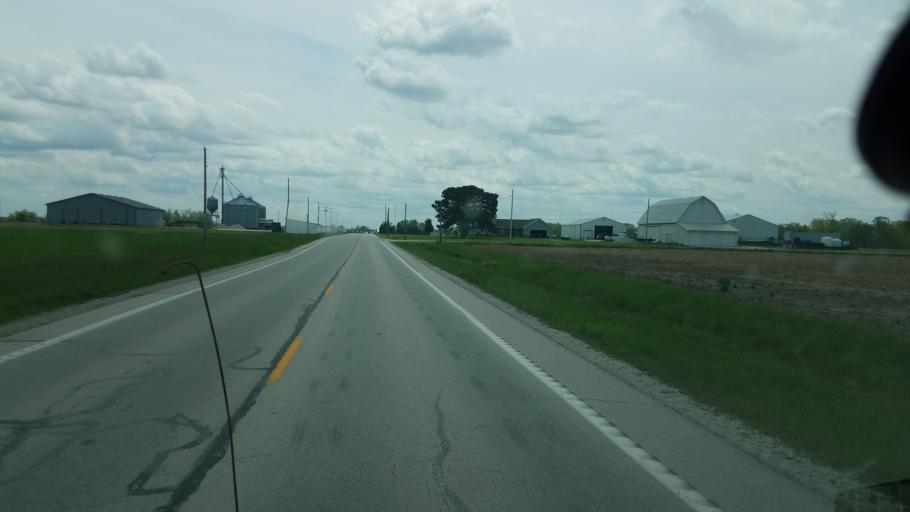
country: US
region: Ohio
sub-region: Sandusky County
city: Ballville
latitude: 41.2489
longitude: -83.1677
